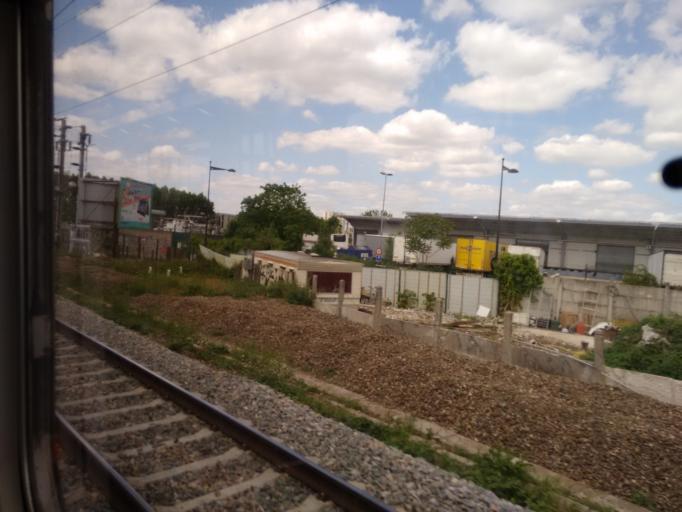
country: FR
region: Ile-de-France
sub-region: Departement de Seine-Saint-Denis
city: Le Bourget
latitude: 48.9329
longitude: 2.4409
